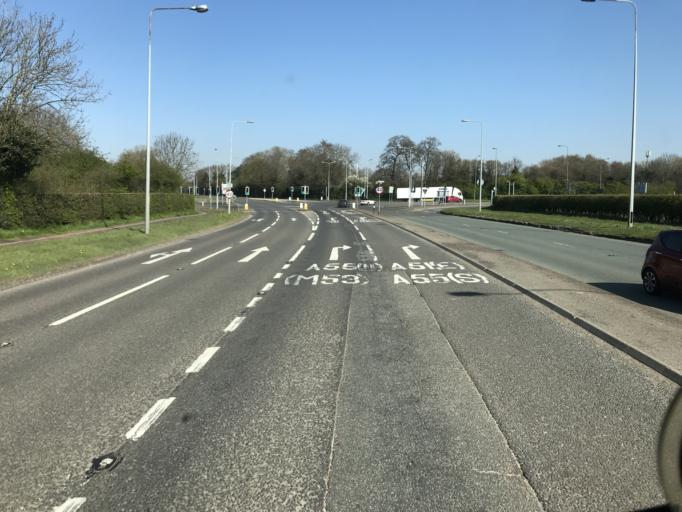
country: GB
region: England
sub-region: Cheshire West and Chester
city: Guilden Sutton
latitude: 53.1936
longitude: -2.8482
